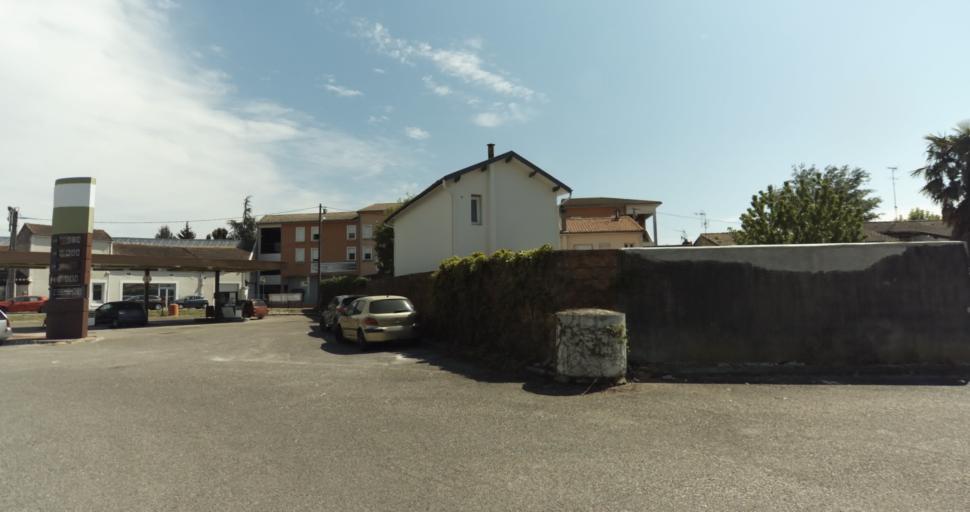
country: FR
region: Aquitaine
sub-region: Departement du Lot-et-Garonne
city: Agen
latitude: 44.2058
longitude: 0.6352
